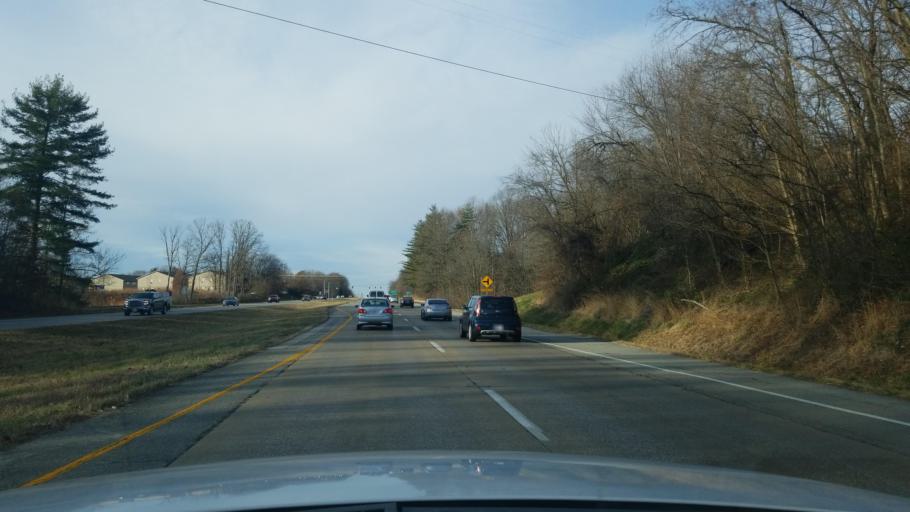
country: US
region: Indiana
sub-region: Vanderburgh County
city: Evansville
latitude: 37.9713
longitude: -87.6590
